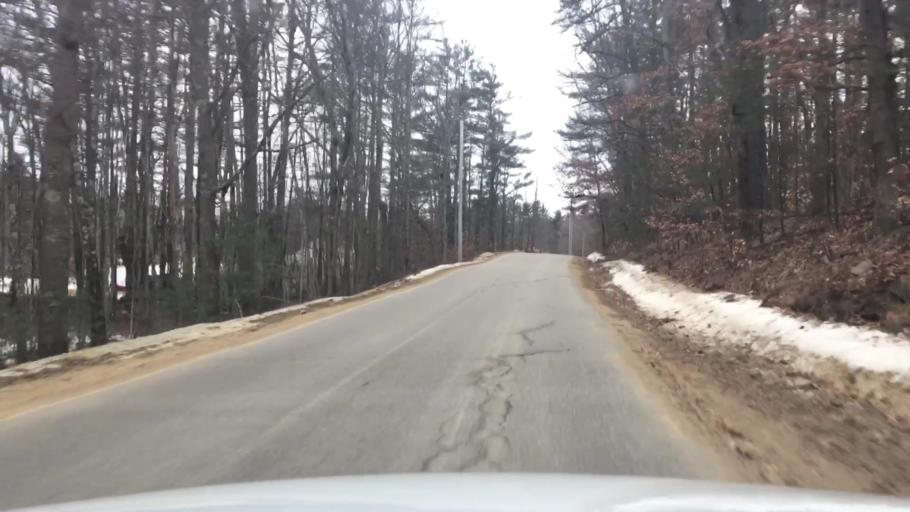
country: US
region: New Hampshire
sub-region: Strafford County
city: Rochester
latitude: 43.3427
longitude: -70.9563
